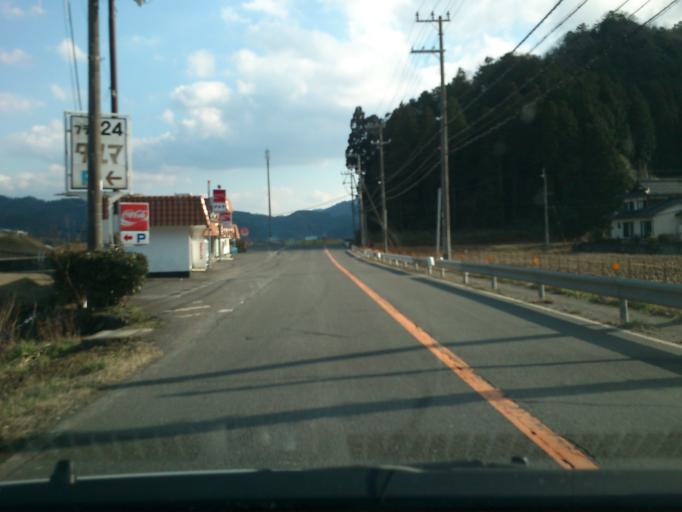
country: JP
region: Kyoto
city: Maizuru
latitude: 35.4713
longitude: 135.2774
